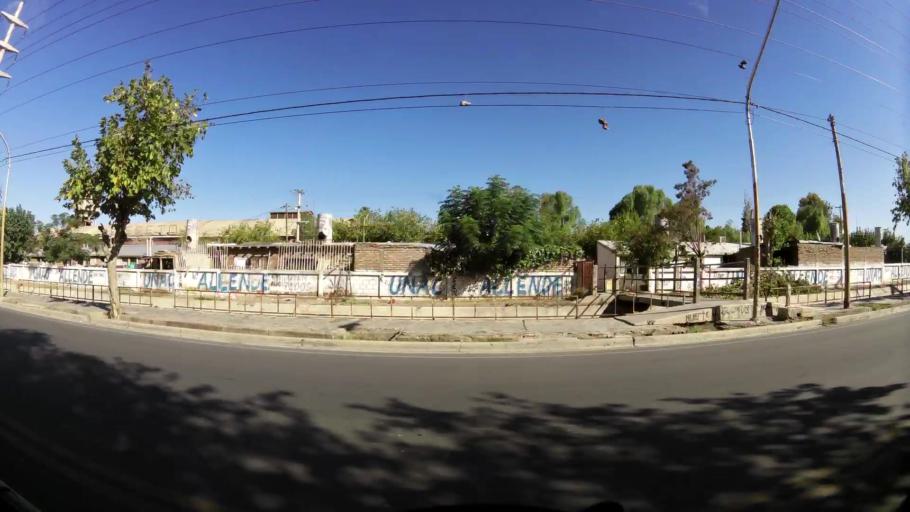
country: AR
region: San Juan
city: Villa Paula de Sarmiento
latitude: -31.5092
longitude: -68.5235
